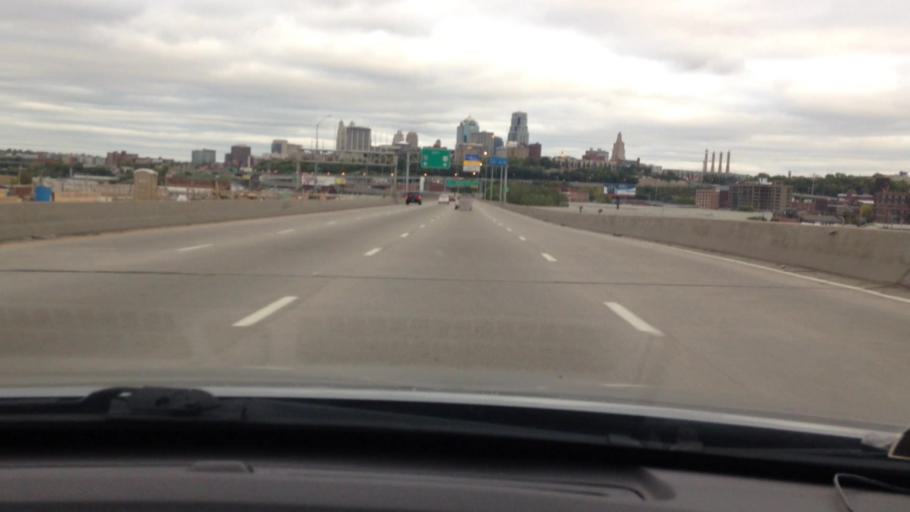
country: US
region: Kansas
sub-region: Wyandotte County
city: Kansas City
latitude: 39.1092
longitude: -94.6088
